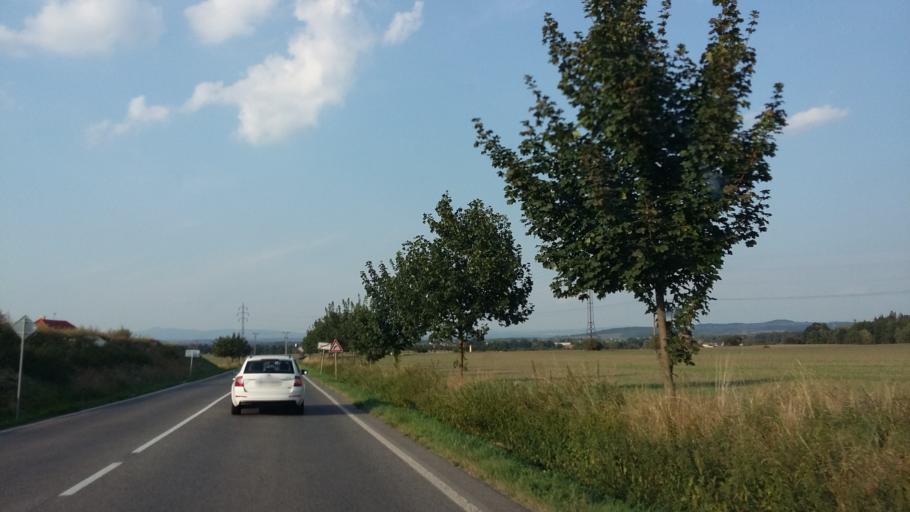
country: CZ
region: Central Bohemia
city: Kosmonosy
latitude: 50.4605
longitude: 14.9318
